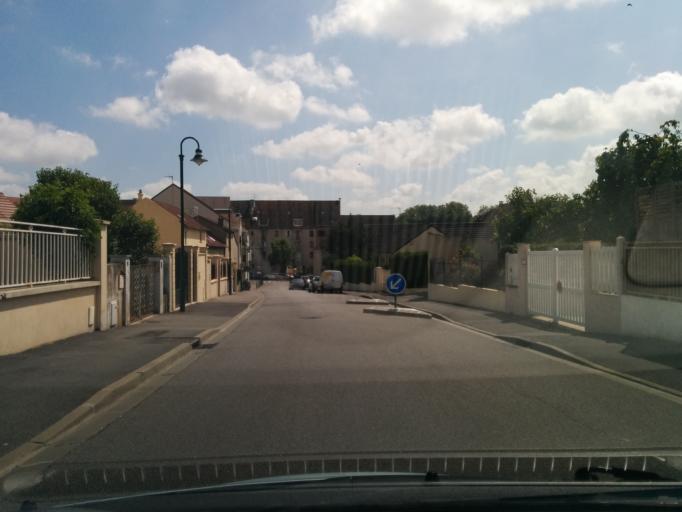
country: FR
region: Ile-de-France
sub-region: Departement des Yvelines
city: Mantes-la-Ville
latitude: 48.9756
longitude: 1.7110
